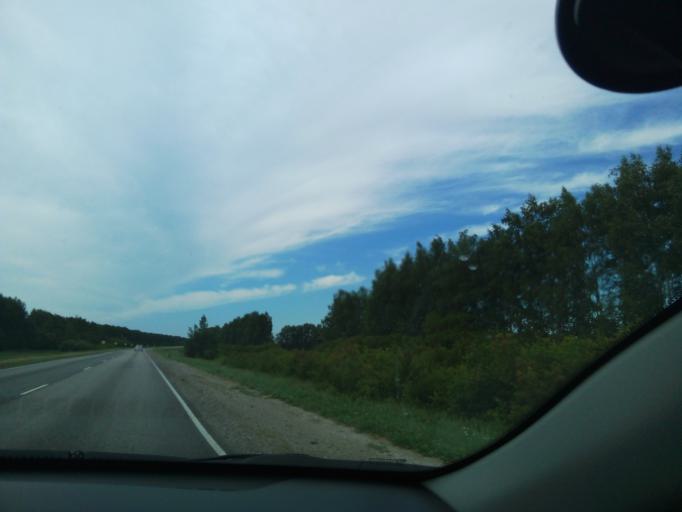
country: RU
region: Tambov
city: Zavoronezhskoye
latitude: 52.6104
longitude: 40.7656
